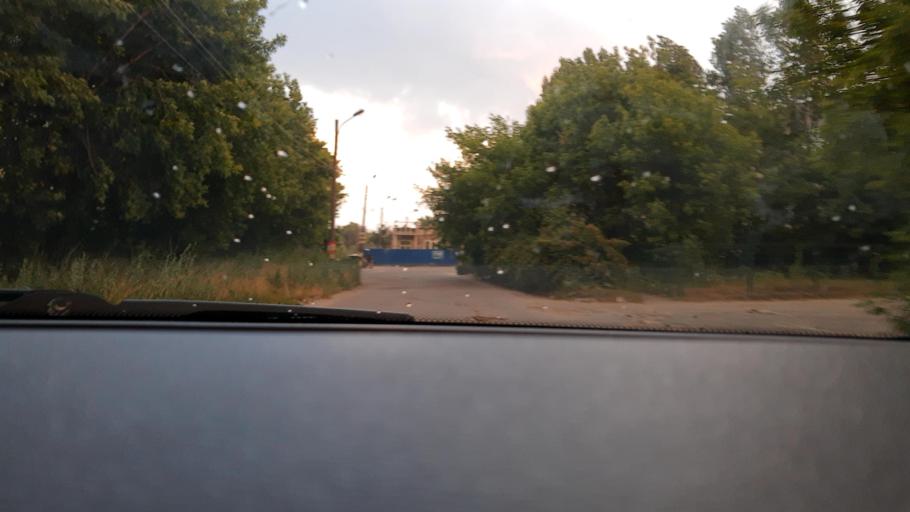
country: RU
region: Nizjnij Novgorod
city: Nizhniy Novgorod
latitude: 56.2942
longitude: 43.9291
